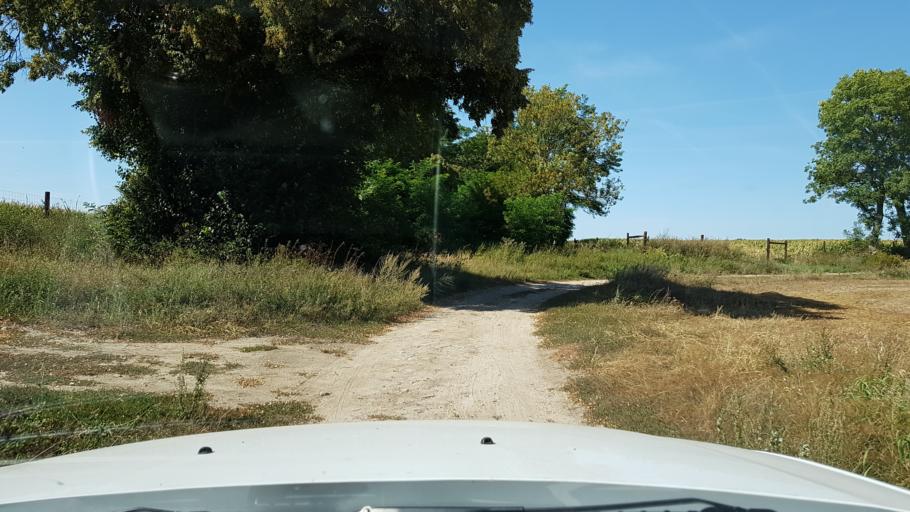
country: PL
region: West Pomeranian Voivodeship
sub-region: Powiat gryfinski
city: Cedynia
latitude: 52.8578
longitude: 14.2241
